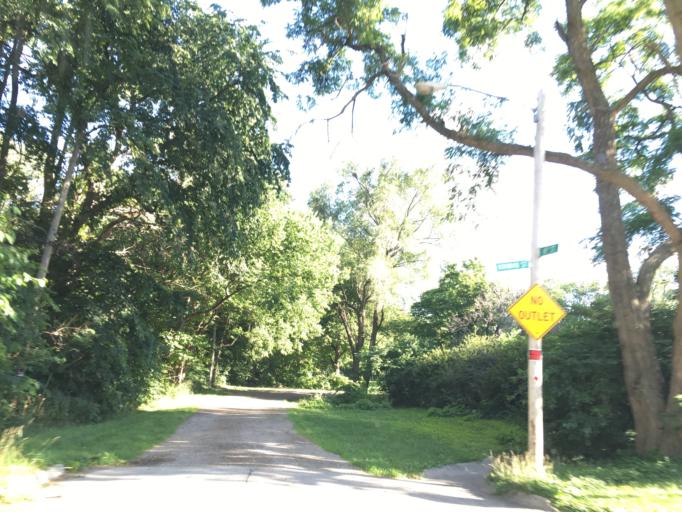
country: US
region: Nebraska
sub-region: Sarpy County
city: La Vista
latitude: 41.1877
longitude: -95.9819
